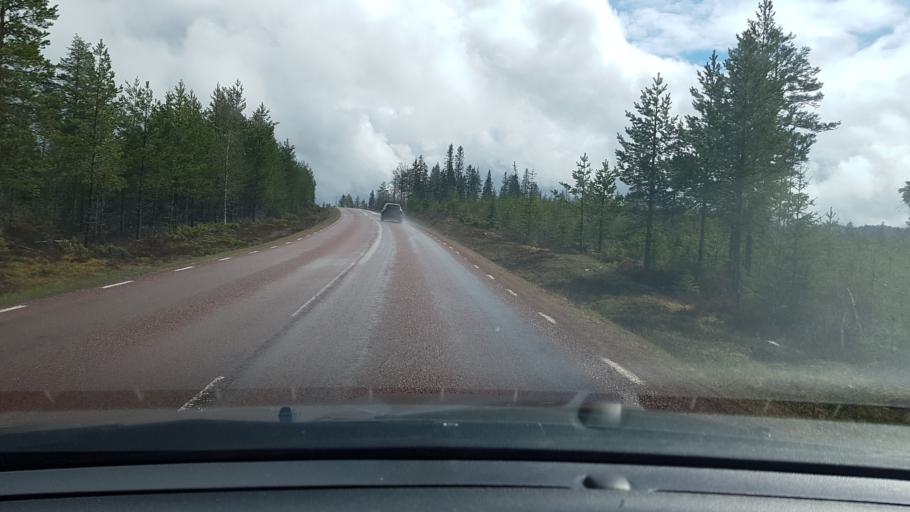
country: SE
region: Dalarna
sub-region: Malung-Saelens kommun
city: Malung
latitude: 61.0510
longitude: 13.3651
